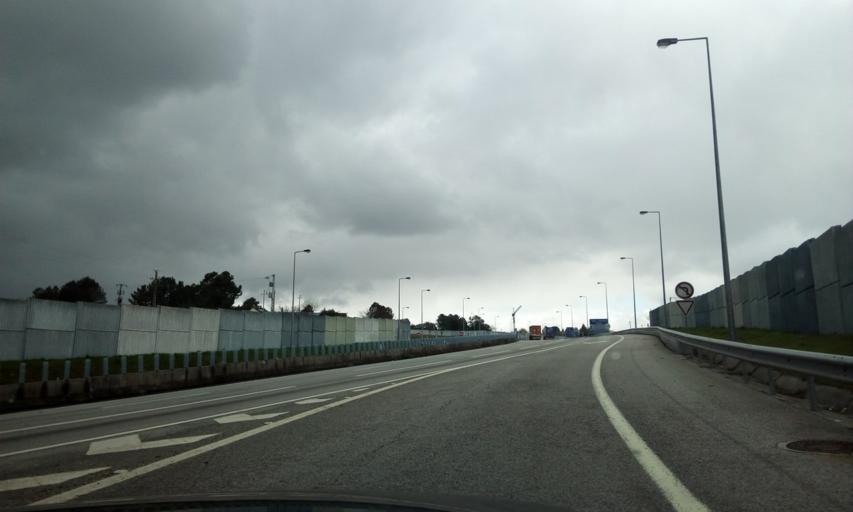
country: PT
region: Viseu
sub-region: Viseu
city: Rio de Loba
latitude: 40.6379
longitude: -7.8496
